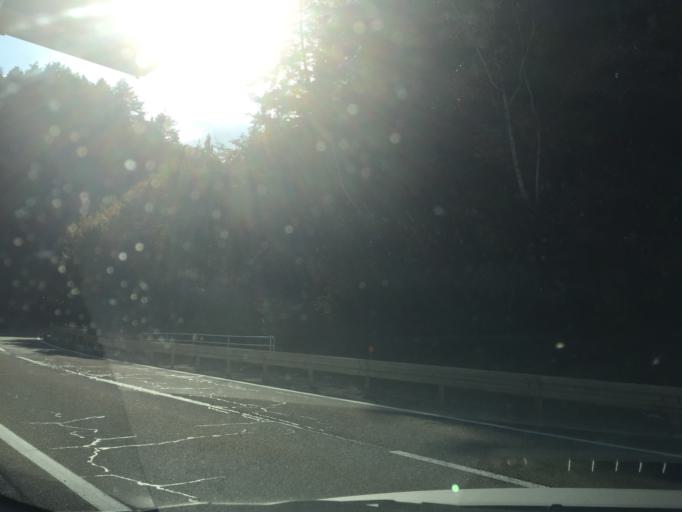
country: JP
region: Nagano
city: Iida
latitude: 35.3793
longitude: 137.6838
